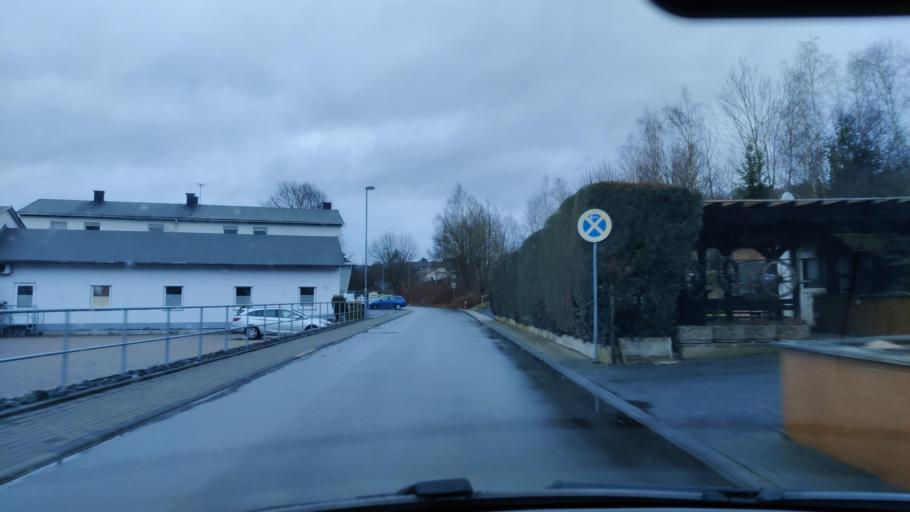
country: DE
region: Hesse
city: Dillenburg
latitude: 50.8178
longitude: 8.3395
